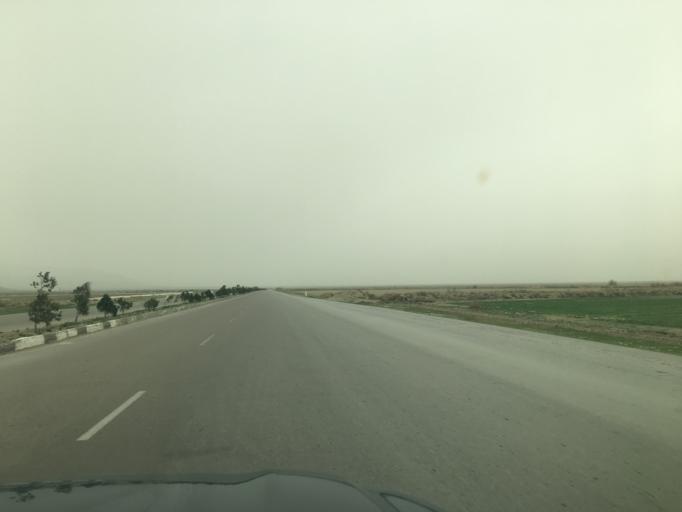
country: TM
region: Ahal
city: Baharly
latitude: 38.3298
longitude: 57.5816
